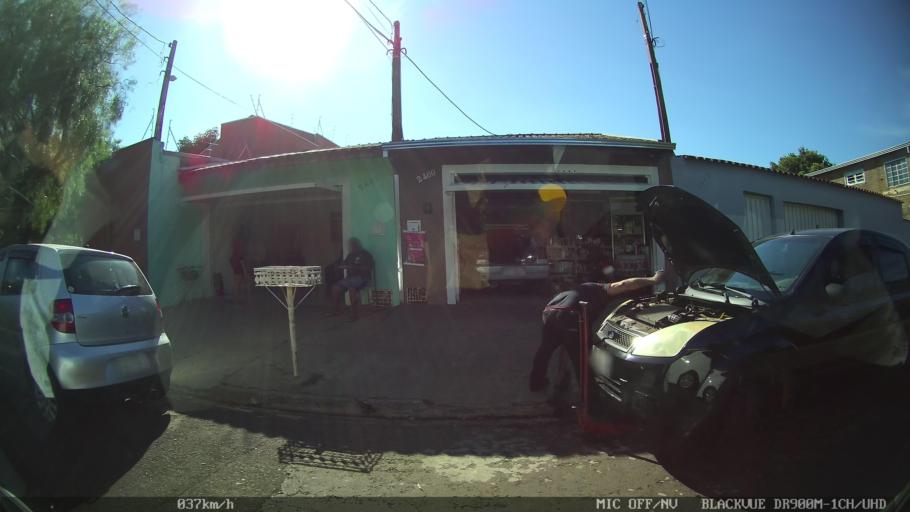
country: BR
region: Sao Paulo
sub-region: Franca
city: Franca
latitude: -20.4916
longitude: -47.4265
